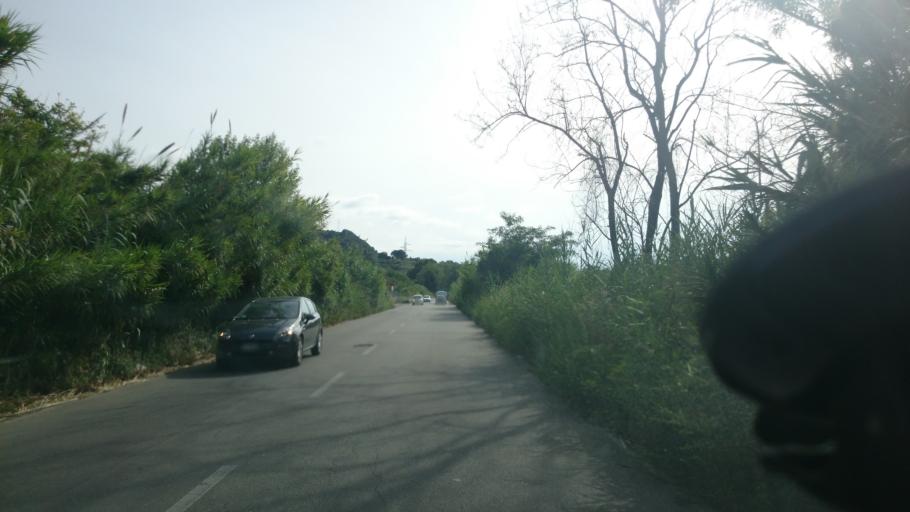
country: IT
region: Calabria
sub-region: Provincia di Vibo-Valentia
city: Sant'Onofrio
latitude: 38.7088
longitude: 16.1192
